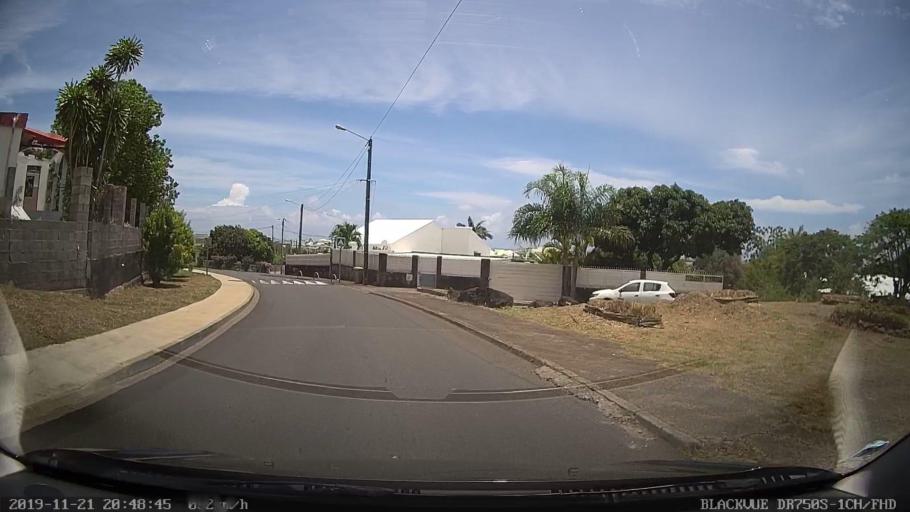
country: RE
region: Reunion
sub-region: Reunion
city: Saint-Denis
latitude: -20.8951
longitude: 55.4659
